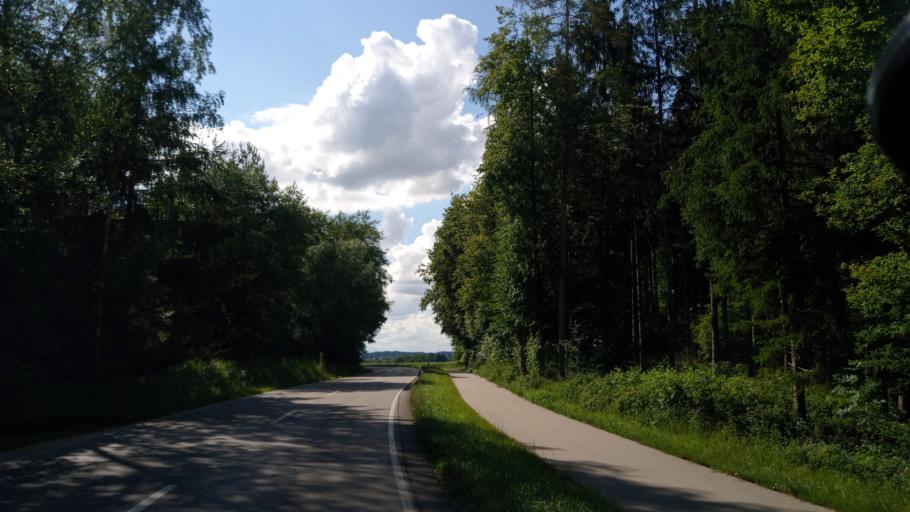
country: DE
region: Bavaria
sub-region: Upper Bavaria
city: Weichs
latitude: 48.3539
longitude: 11.4114
